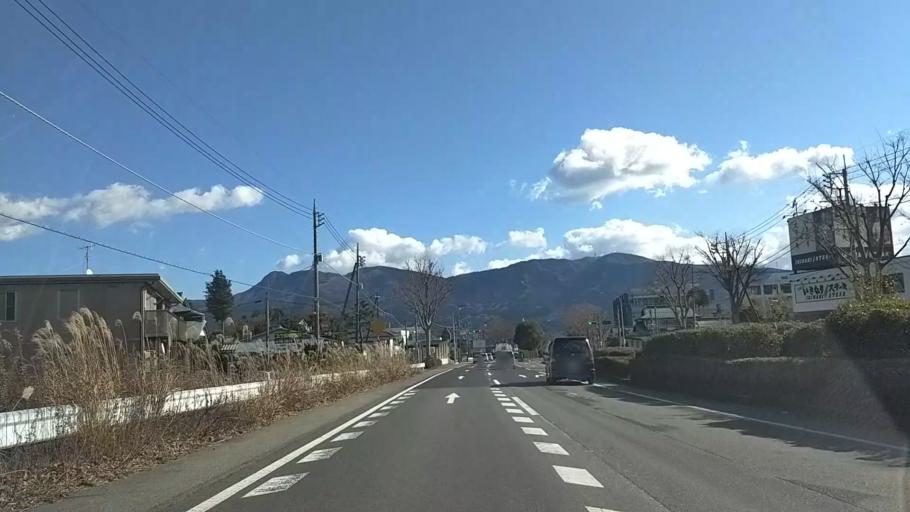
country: JP
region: Shizuoka
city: Gotemba
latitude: 35.3107
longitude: 138.9335
